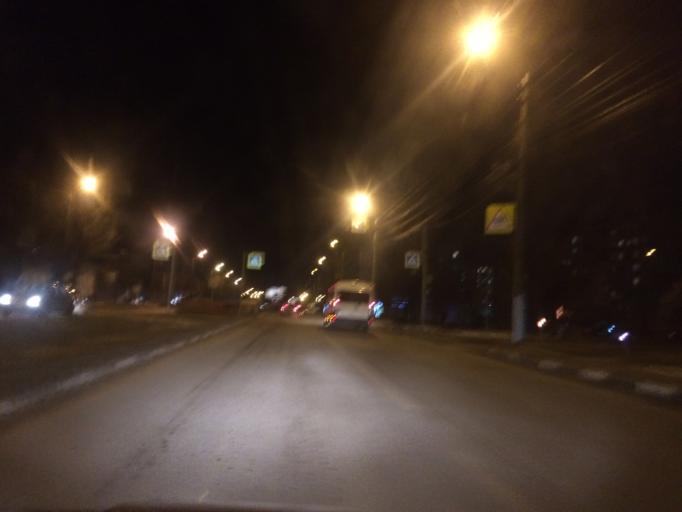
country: RU
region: Tula
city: Tula
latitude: 54.2051
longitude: 37.6864
